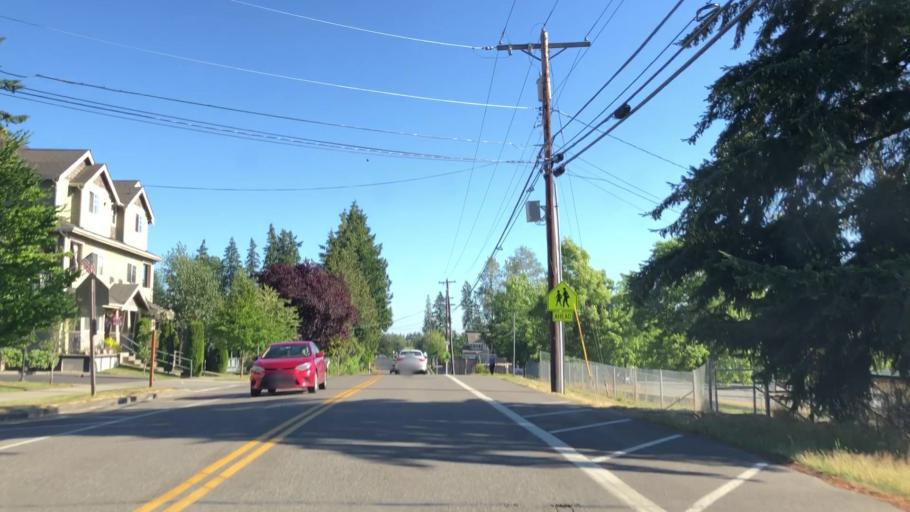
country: US
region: Washington
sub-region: Snohomish County
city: Martha Lake
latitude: 47.8583
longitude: -122.2579
